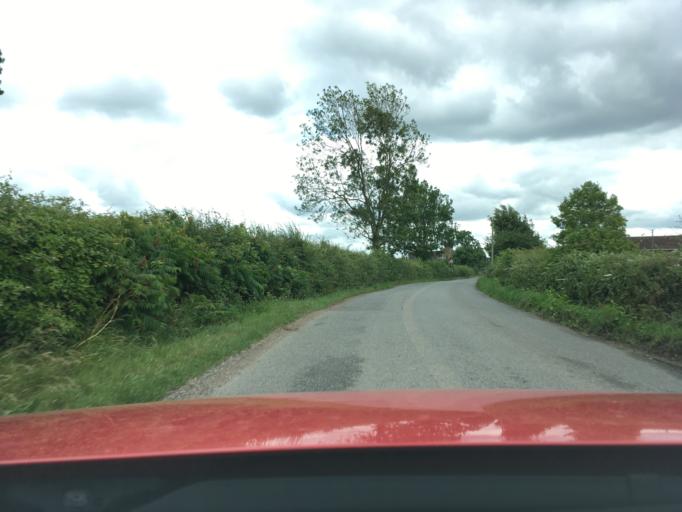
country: GB
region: England
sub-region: Gloucestershire
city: Stonehouse
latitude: 51.8054
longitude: -2.3432
